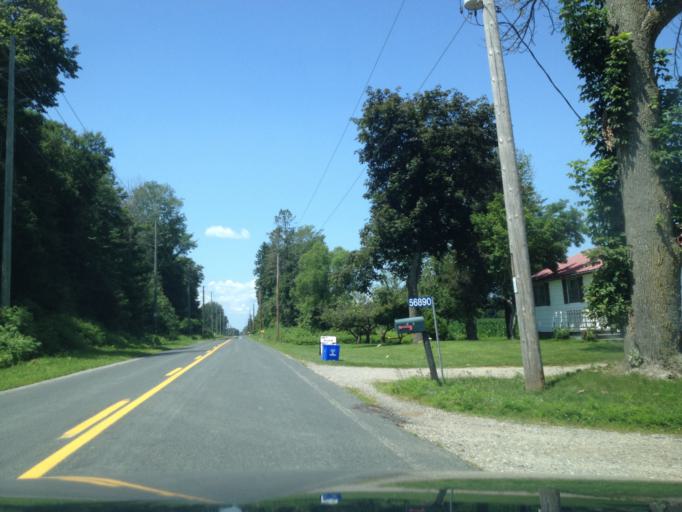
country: CA
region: Ontario
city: Aylmer
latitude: 42.6452
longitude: -80.7470
